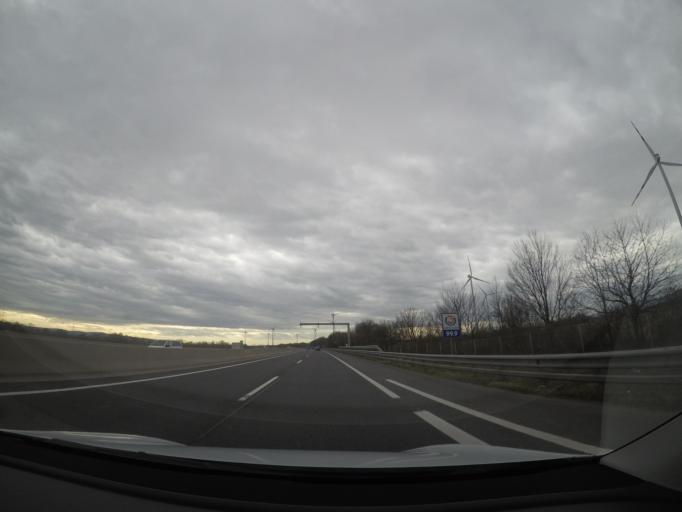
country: AT
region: Lower Austria
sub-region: Politischer Bezirk Baden
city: Ebreichsdorf
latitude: 47.9601
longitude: 16.3660
